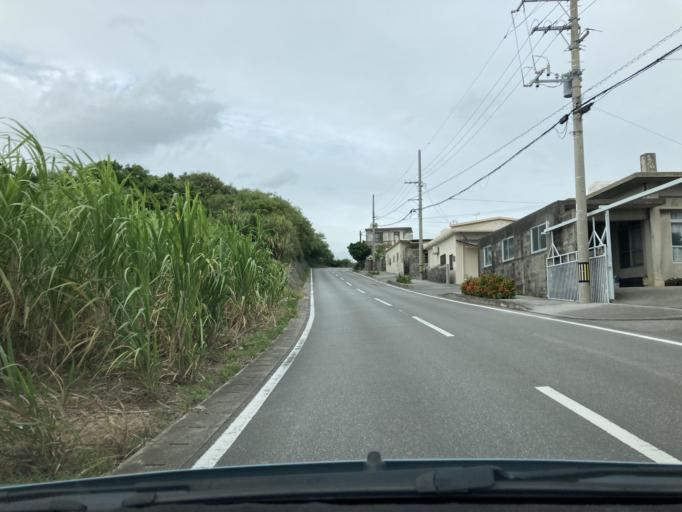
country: JP
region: Okinawa
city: Tomigusuku
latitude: 26.1544
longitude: 127.6984
